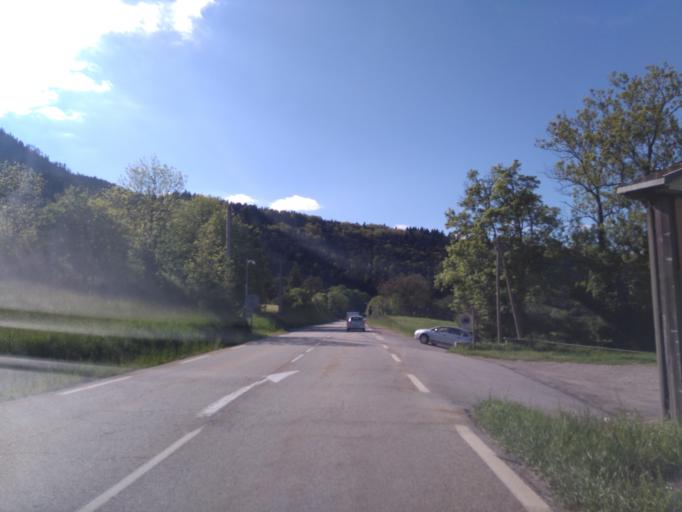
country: FR
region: Rhone-Alpes
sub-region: Departement de l'Isere
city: Mens
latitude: 44.7615
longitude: 5.6622
